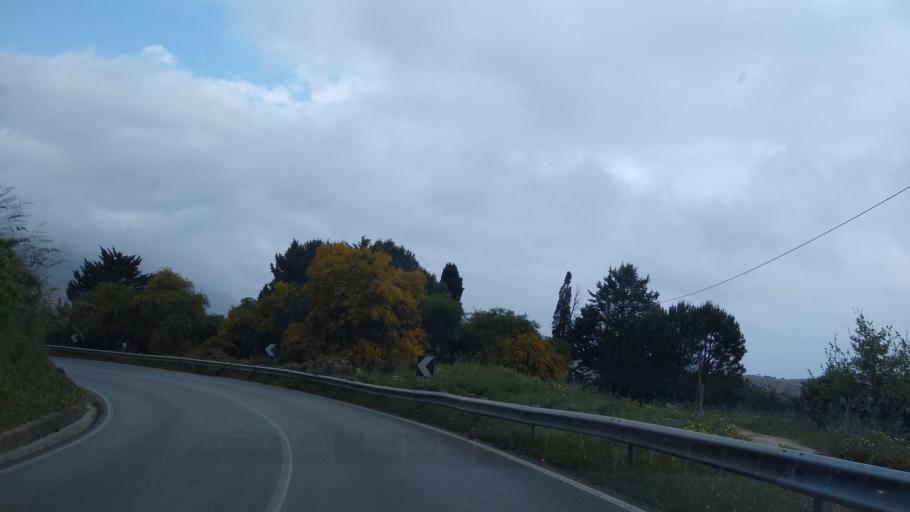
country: IT
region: Sicily
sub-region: Trapani
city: Alcamo
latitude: 37.9785
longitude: 12.9385
